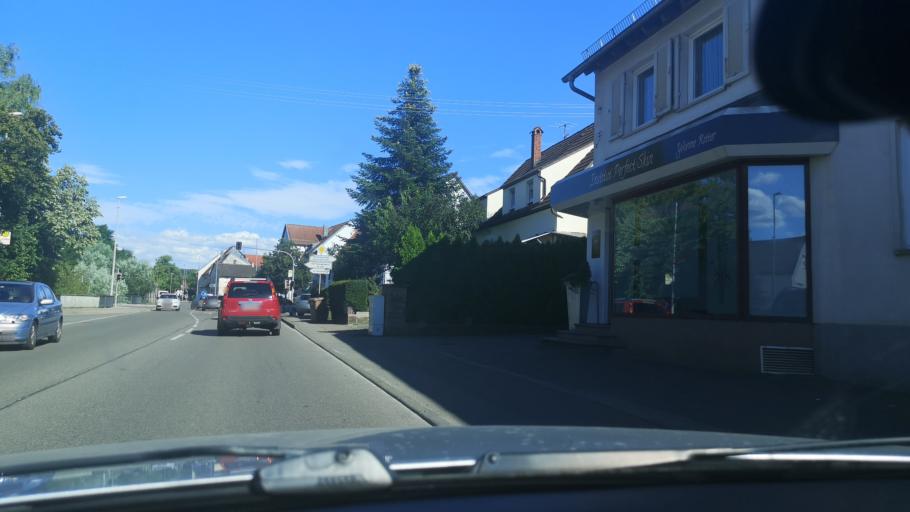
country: DE
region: Baden-Wuerttemberg
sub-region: Regierungsbezirk Stuttgart
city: Kirchheim unter Teck
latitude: 48.6398
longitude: 9.4826
